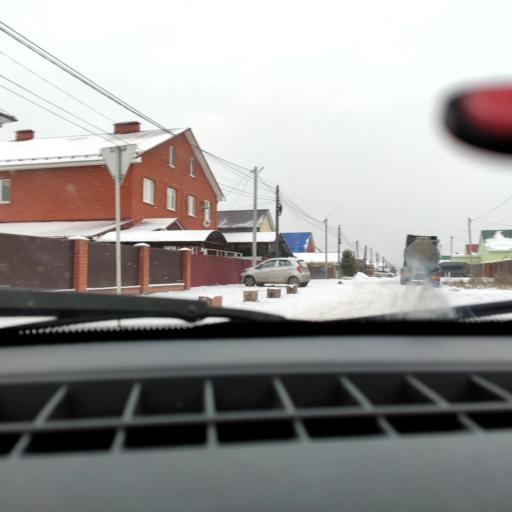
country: RU
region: Bashkortostan
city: Ufa
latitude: 54.6286
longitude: 55.9141
